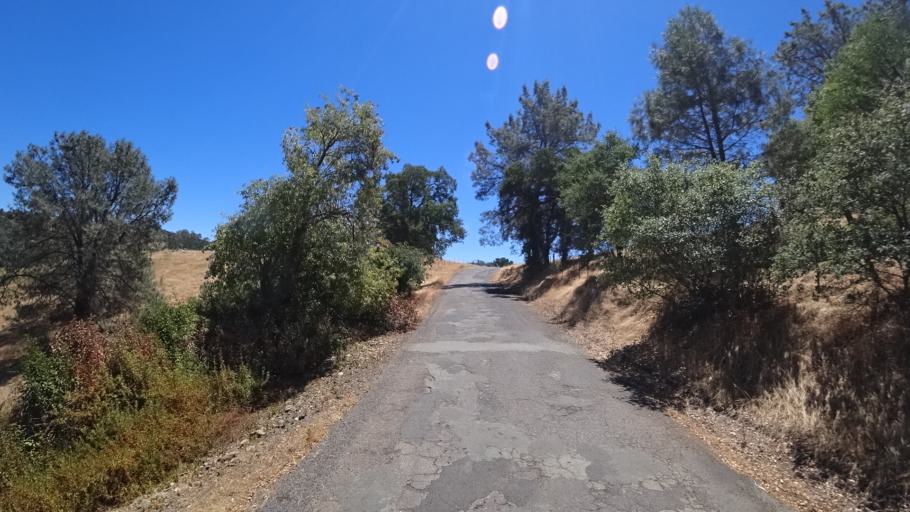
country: US
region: California
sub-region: Calaveras County
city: Rancho Calaveras
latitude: 38.0545
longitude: -120.8027
